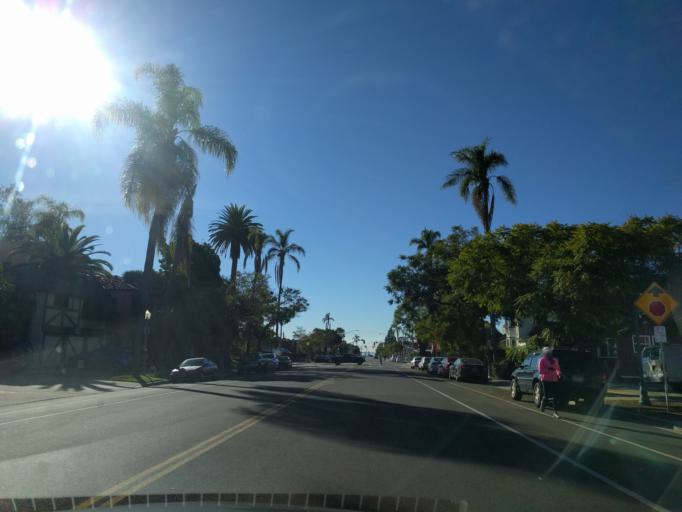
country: US
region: California
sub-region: San Diego County
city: San Diego
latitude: 32.7187
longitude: -117.1404
